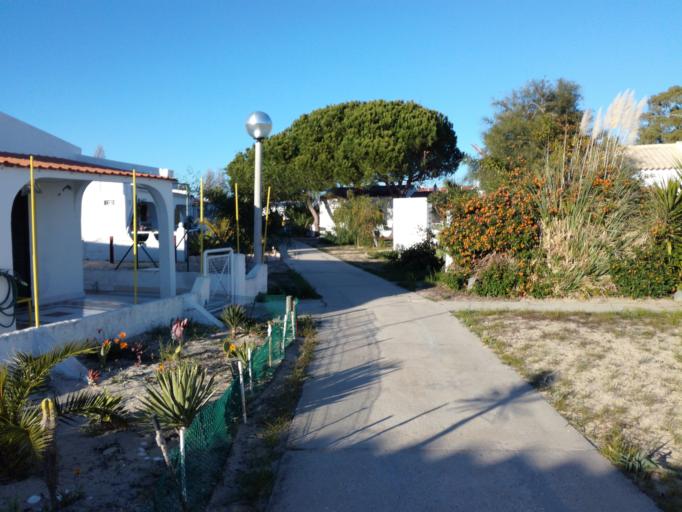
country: PT
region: Faro
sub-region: Olhao
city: Olhao
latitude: 37.0175
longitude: -7.8023
